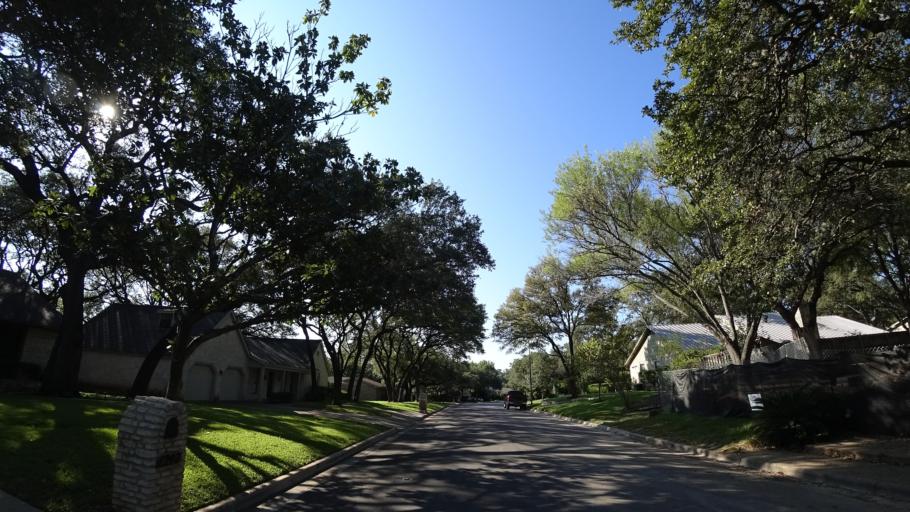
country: US
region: Texas
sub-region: Travis County
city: Rollingwood
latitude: 30.2687
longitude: -97.7981
